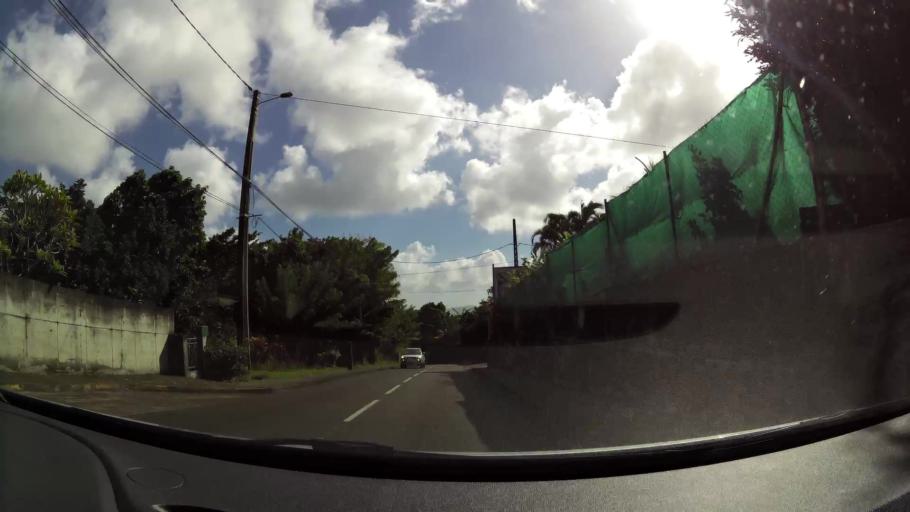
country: MQ
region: Martinique
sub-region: Martinique
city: Fort-de-France
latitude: 14.6298
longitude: -61.0599
